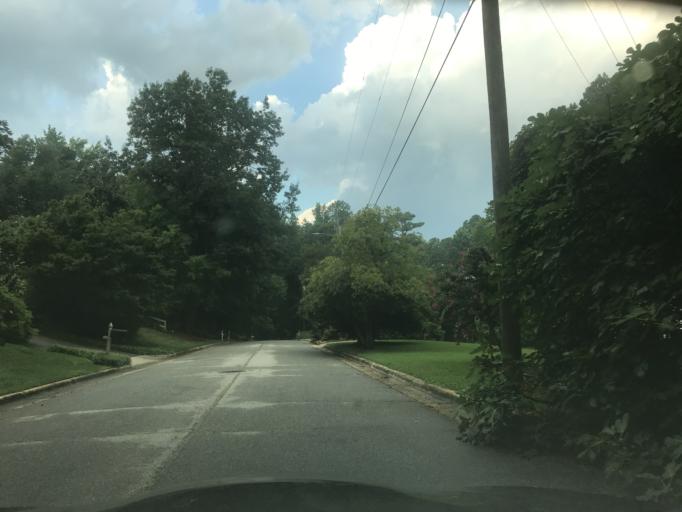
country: US
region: North Carolina
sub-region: Wake County
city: West Raleigh
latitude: 35.8341
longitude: -78.6625
